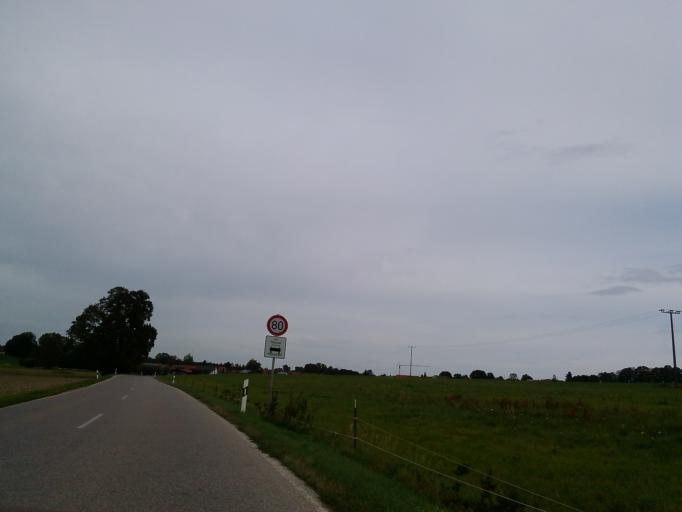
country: DE
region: Bavaria
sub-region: Upper Bavaria
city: Gilching
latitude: 48.0594
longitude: 11.3214
